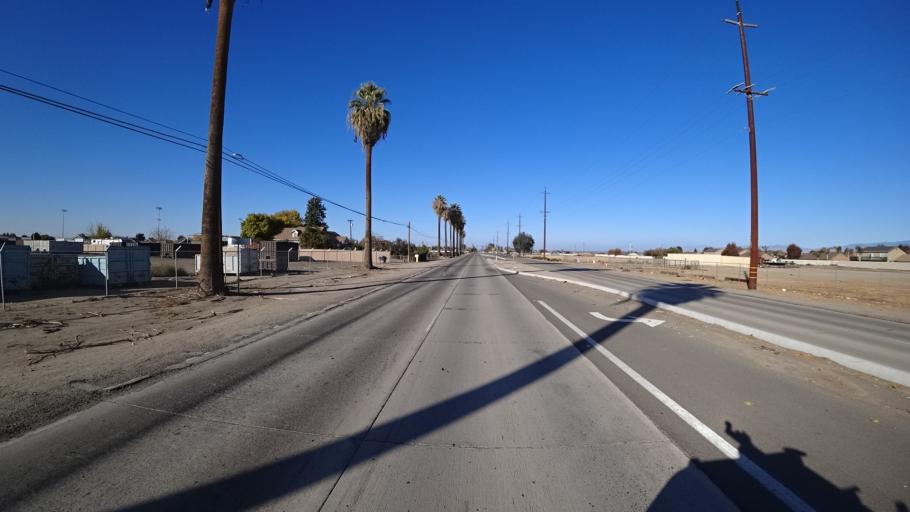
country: US
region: California
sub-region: Kern County
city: Greenfield
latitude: 35.2780
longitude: -119.0031
